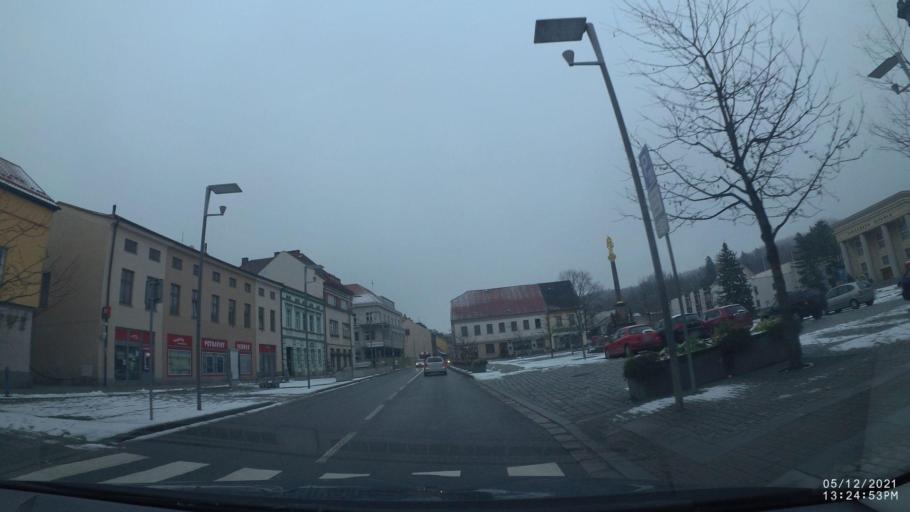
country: CZ
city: Hronov
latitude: 50.4796
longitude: 16.1816
